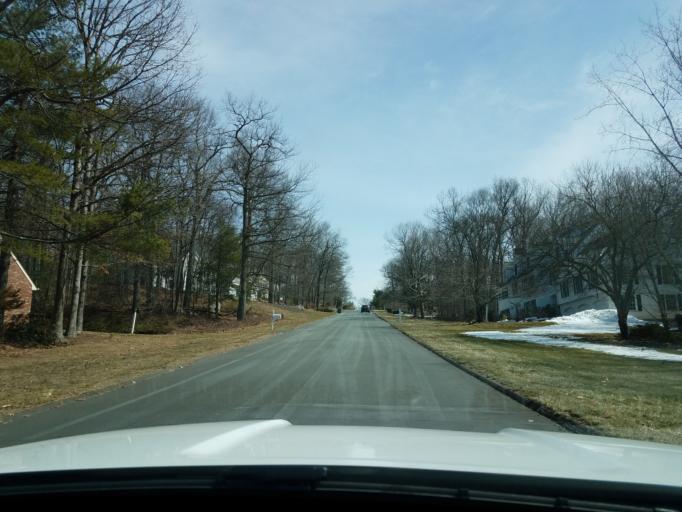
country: US
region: Connecticut
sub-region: Hartford County
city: Collinsville
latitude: 41.7861
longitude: -72.9041
